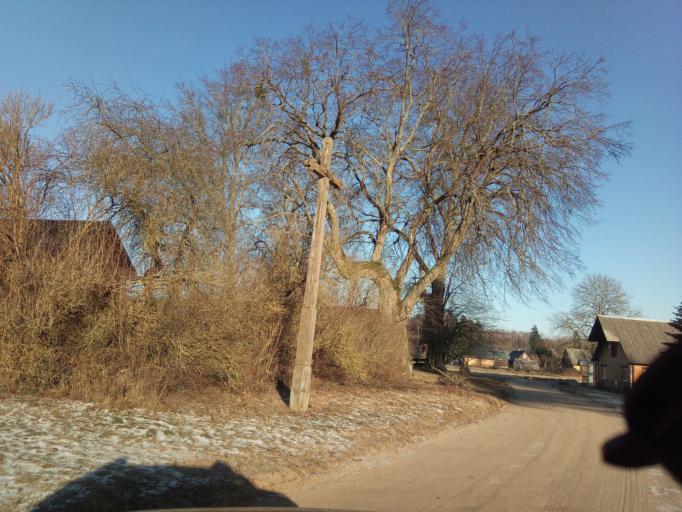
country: LT
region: Alytaus apskritis
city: Druskininkai
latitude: 53.9536
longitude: 23.8876
